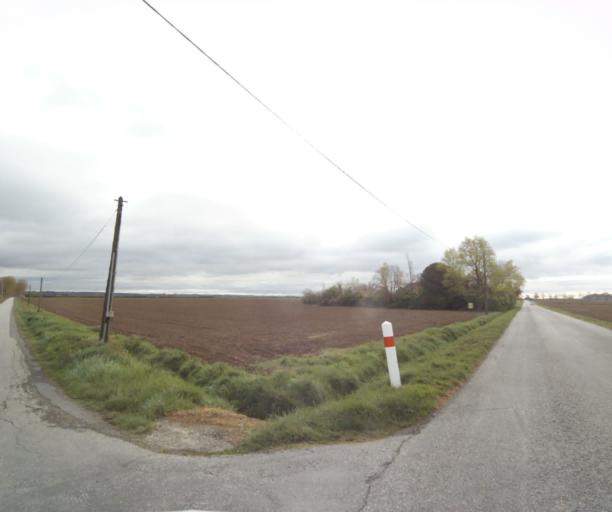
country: FR
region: Midi-Pyrenees
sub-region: Departement de l'Ariege
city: Saverdun
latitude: 43.2559
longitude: 1.5398
